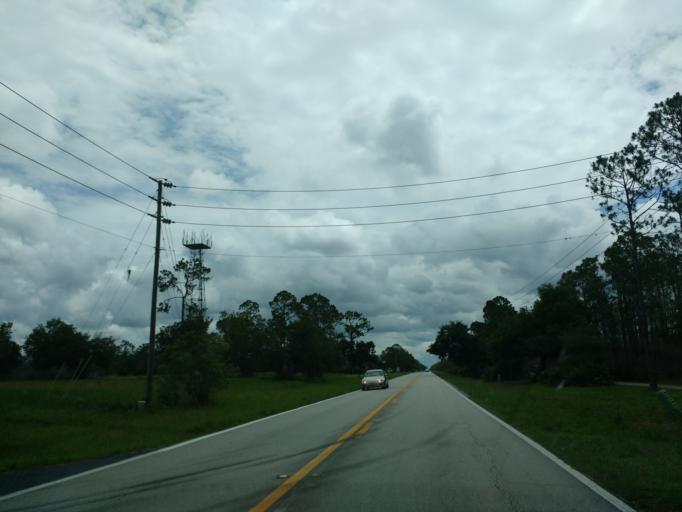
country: US
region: Florida
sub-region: Highlands County
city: Sebring
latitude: 27.4709
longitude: -81.5130
